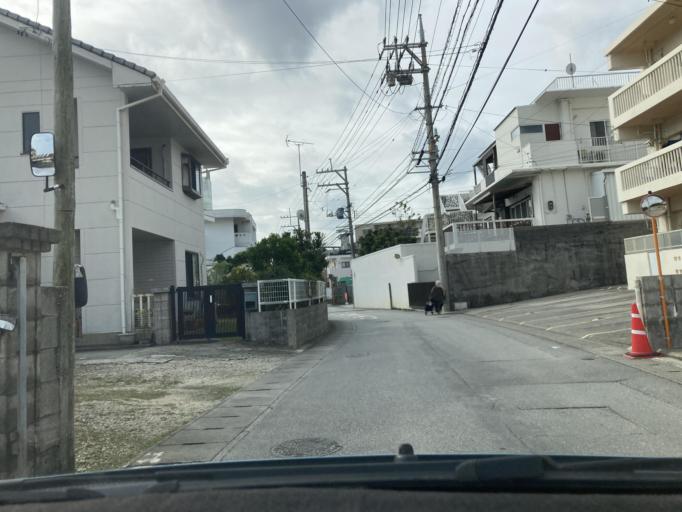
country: JP
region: Okinawa
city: Ginowan
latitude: 26.2049
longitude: 127.7531
